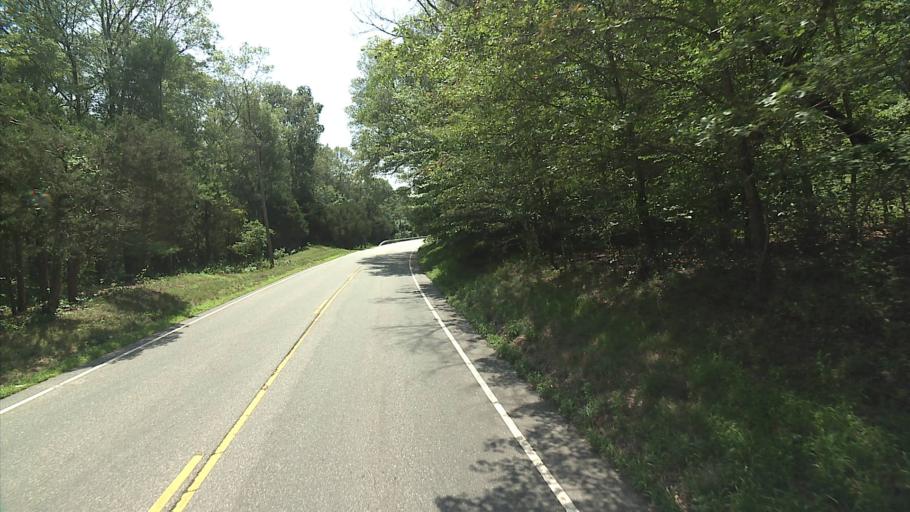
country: US
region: Connecticut
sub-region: New London County
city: Preston City
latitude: 41.5374
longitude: -71.9253
